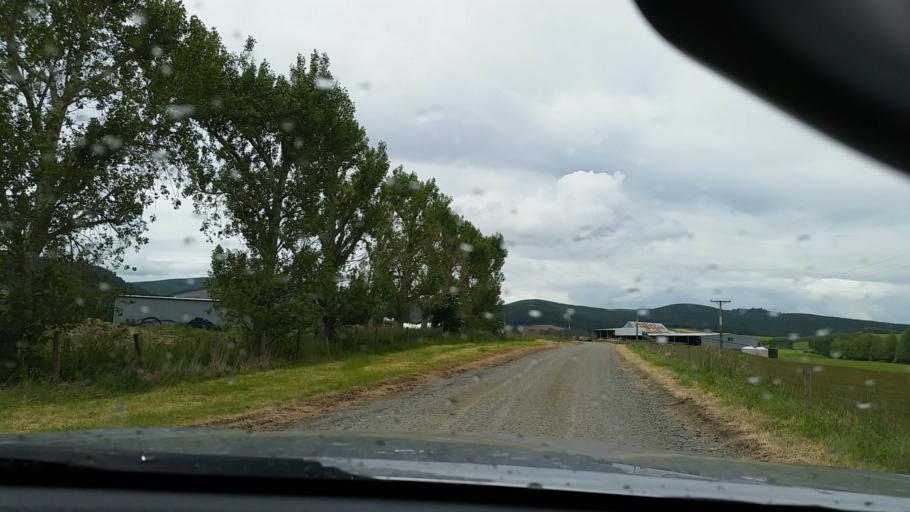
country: NZ
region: Southland
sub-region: Southland District
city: Winton
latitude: -45.9078
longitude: 168.1472
